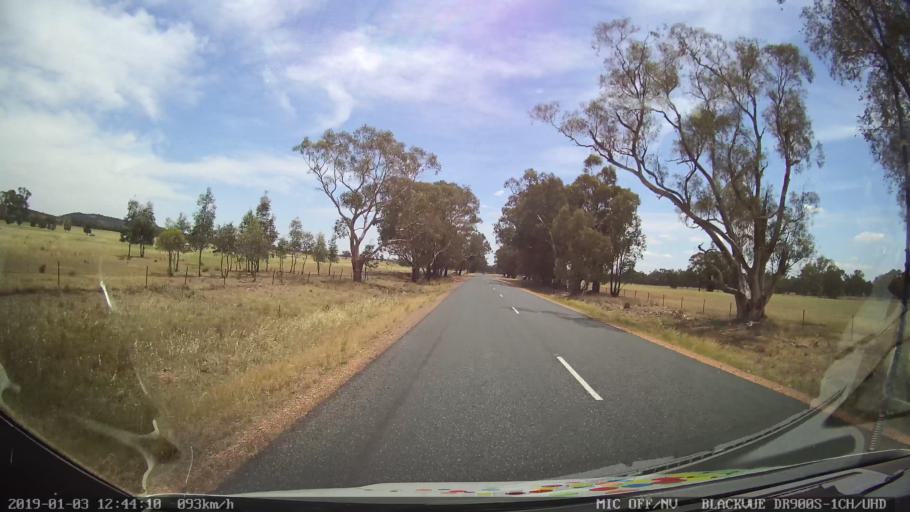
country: AU
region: New South Wales
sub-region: Weddin
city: Grenfell
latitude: -33.7652
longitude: 148.2149
